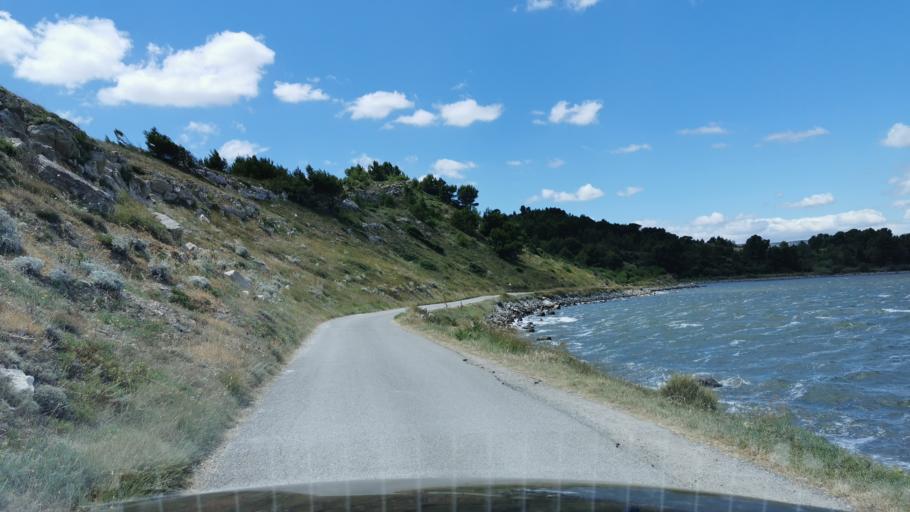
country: FR
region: Languedoc-Roussillon
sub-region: Departement de l'Aude
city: Peyriac-de-Mer
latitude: 43.0874
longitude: 2.9782
